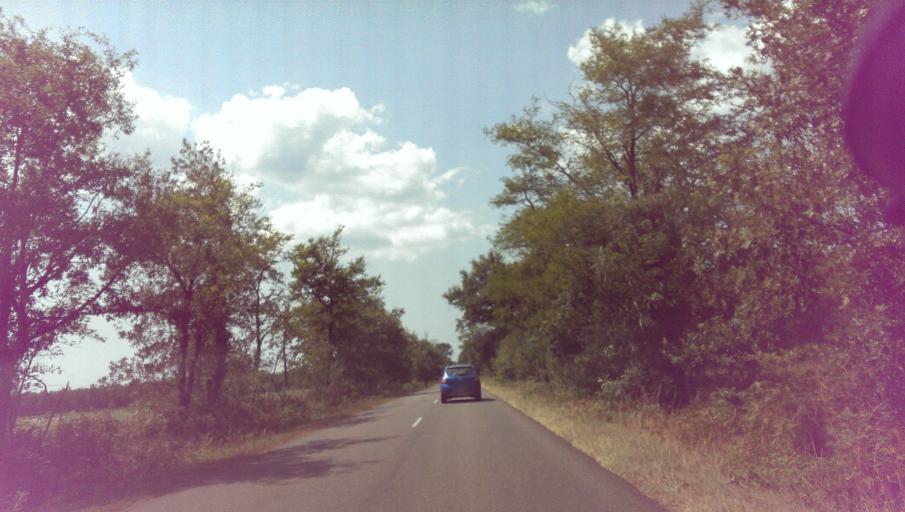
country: FR
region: Aquitaine
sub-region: Departement des Landes
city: Sabres
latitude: 44.1211
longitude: -0.6561
